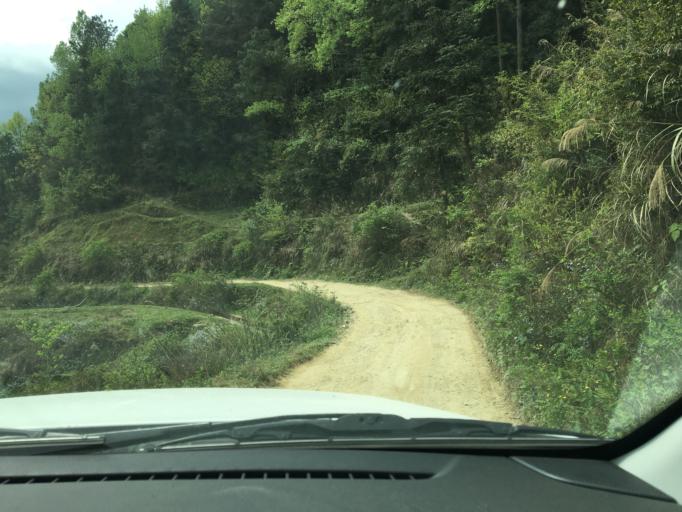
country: CN
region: Guizhou Sheng
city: Kuanping
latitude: 28.0243
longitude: 108.0544
